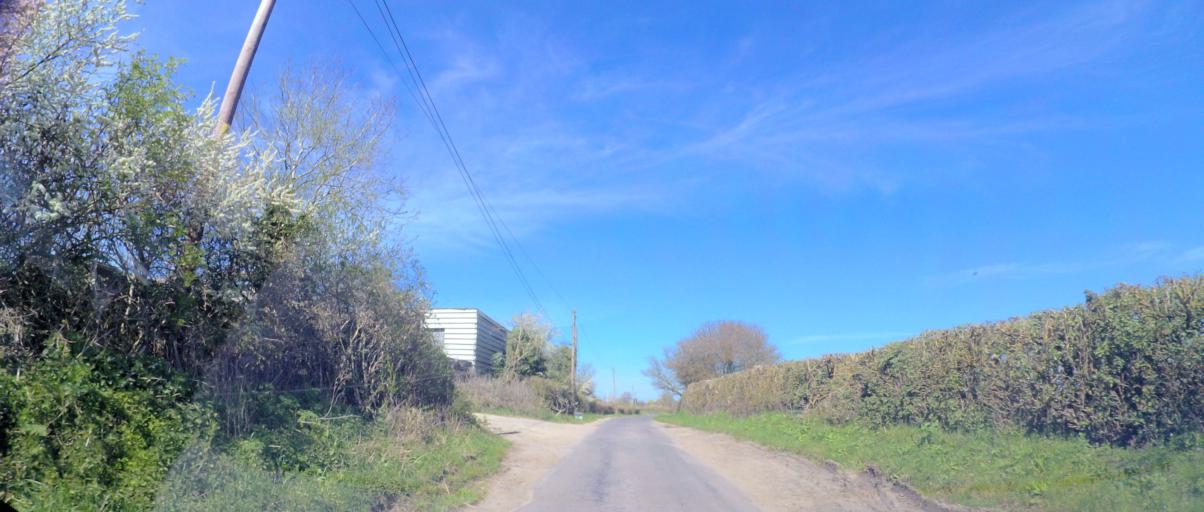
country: GB
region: England
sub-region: West Berkshire
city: Stratfield Mortimer
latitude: 51.3869
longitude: -1.0006
